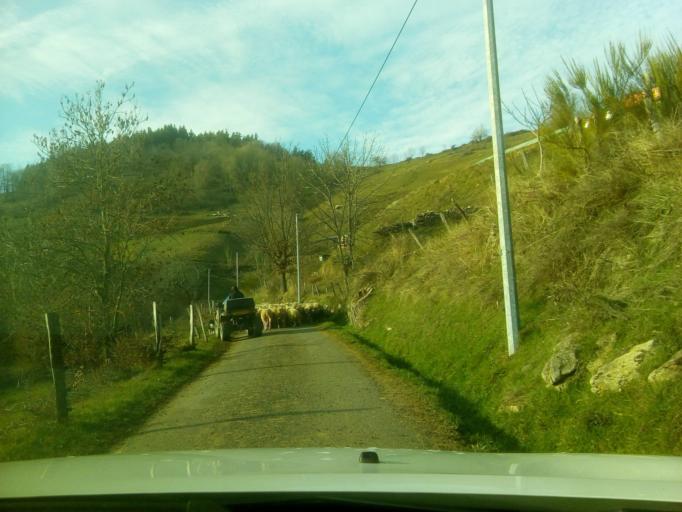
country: FR
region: Rhone-Alpes
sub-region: Departement de l'Ardeche
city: Saint-Martin-de-Valamas
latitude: 44.8973
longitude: 4.3545
